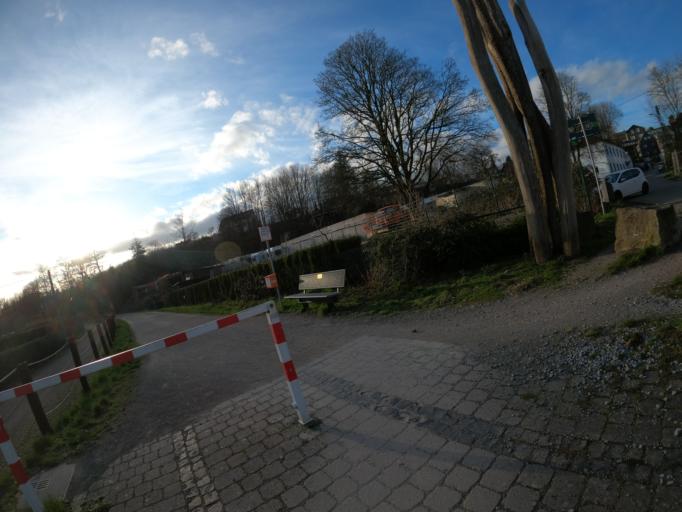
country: DE
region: North Rhine-Westphalia
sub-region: Regierungsbezirk Dusseldorf
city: Wuppertal
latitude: 51.2267
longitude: 7.1341
